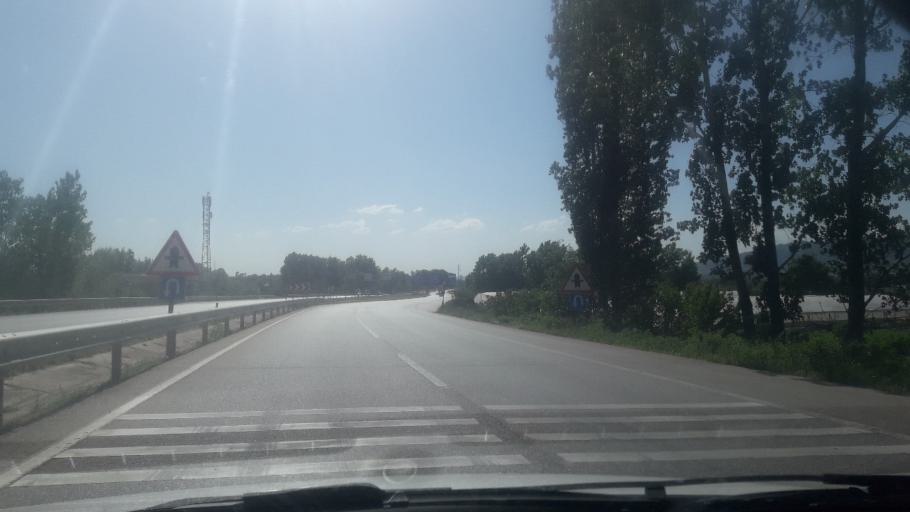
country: TR
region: Tokat
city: Yesilyurt
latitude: 40.2986
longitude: 36.3642
